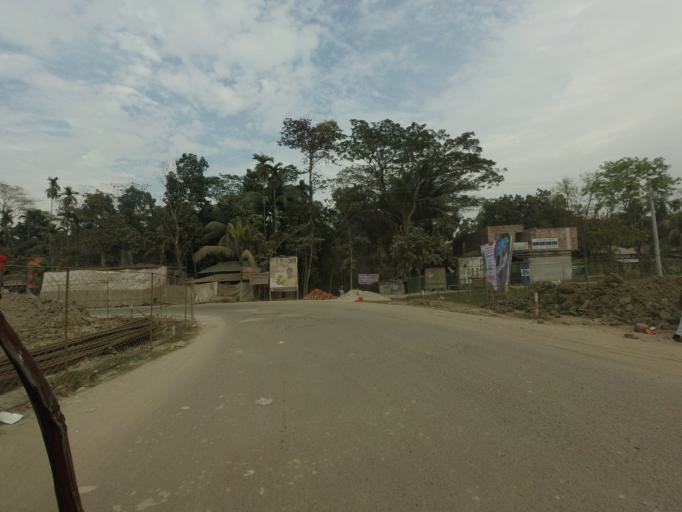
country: BD
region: Barisal
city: Nalchiti
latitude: 22.4597
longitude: 90.3411
